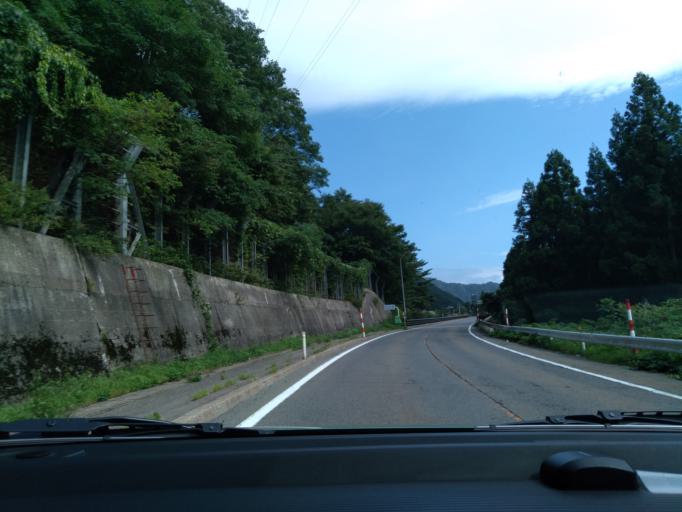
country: JP
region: Akita
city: Kakunodatemachi
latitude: 39.7035
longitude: 140.7531
